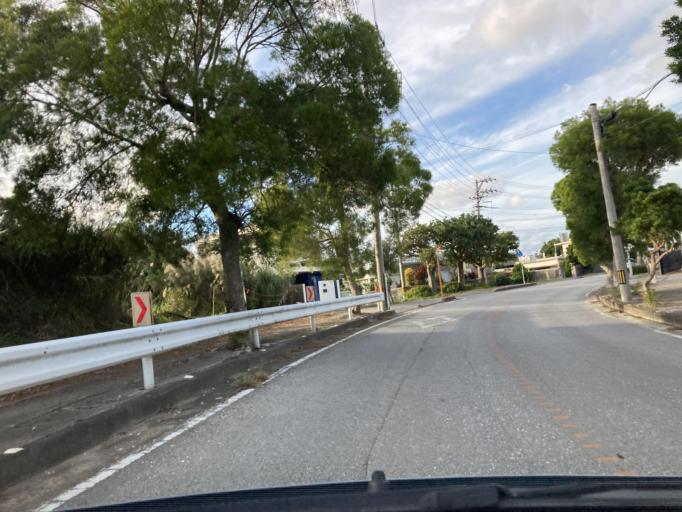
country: JP
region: Okinawa
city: Itoman
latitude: 26.1346
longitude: 127.6987
